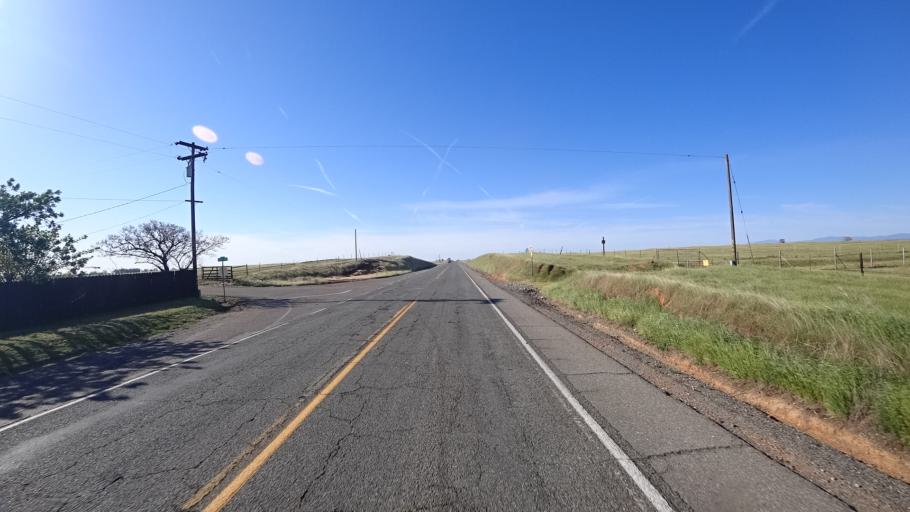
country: US
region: California
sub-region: Glenn County
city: Orland
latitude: 39.8130
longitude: -122.1973
